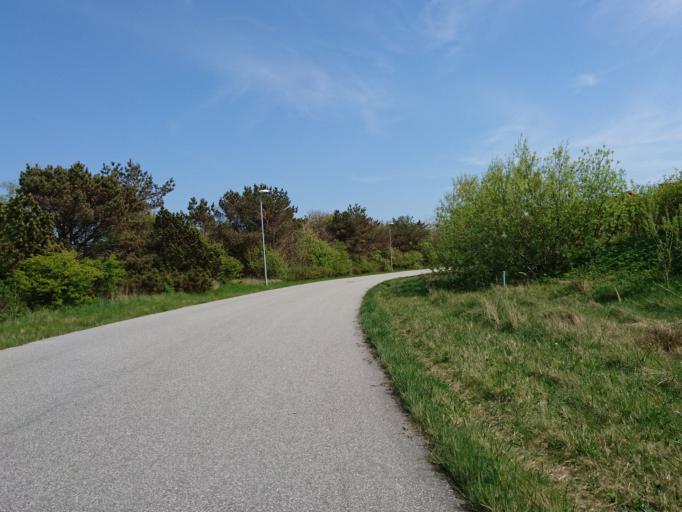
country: DK
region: North Denmark
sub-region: Frederikshavn Kommune
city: Skagen
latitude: 57.7350
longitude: 10.5949
